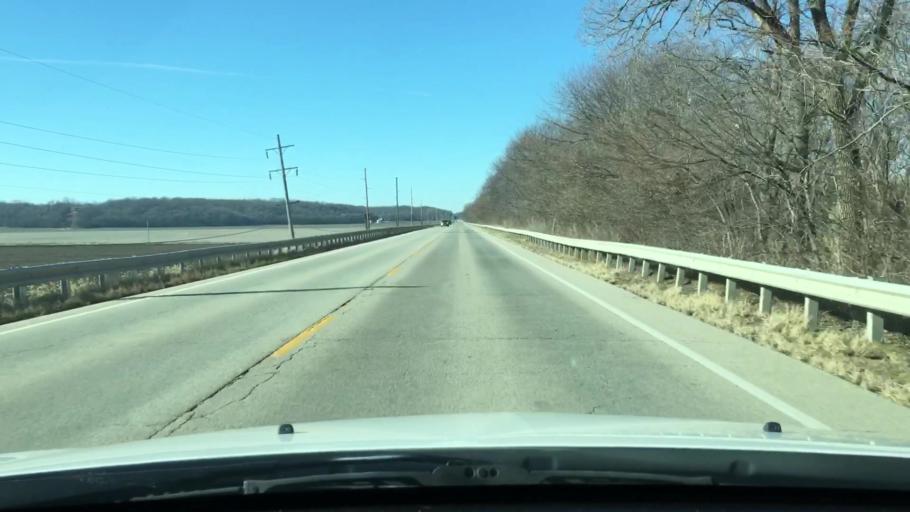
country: US
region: Illinois
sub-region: Mason County
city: Havana
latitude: 40.3008
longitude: -90.1112
